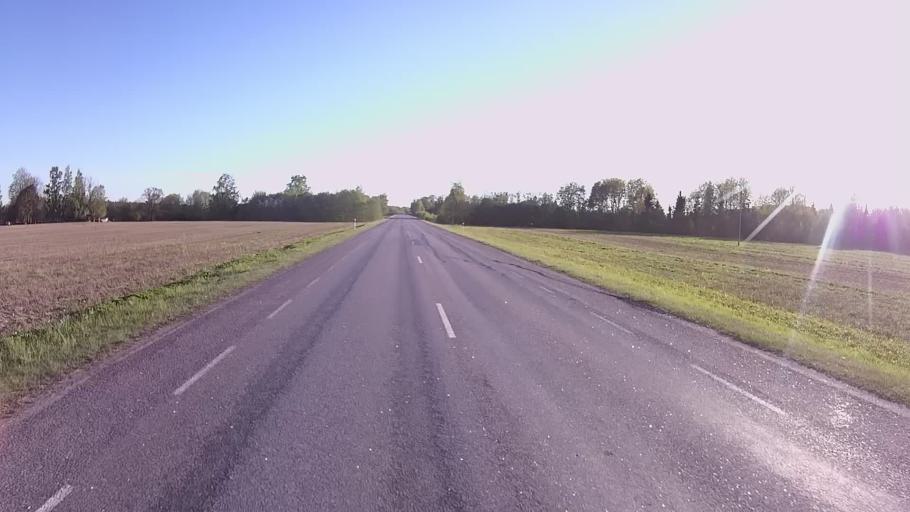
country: EE
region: Viljandimaa
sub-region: Viiratsi vald
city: Viiratsi
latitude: 58.4117
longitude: 25.6807
